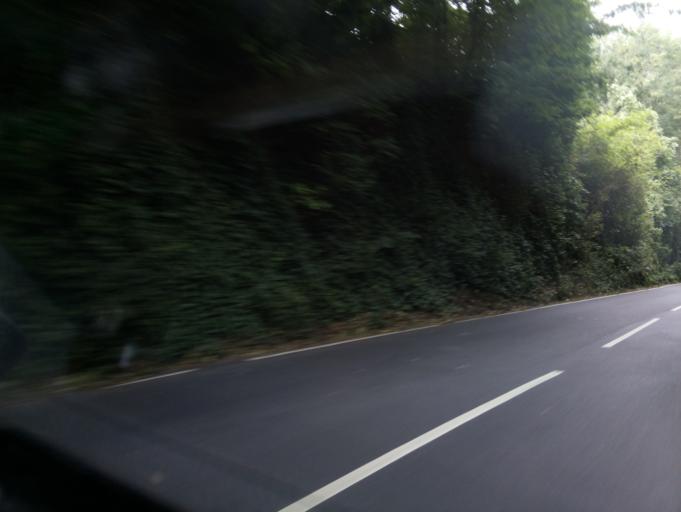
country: GB
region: England
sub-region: Devon
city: Starcross
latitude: 50.6415
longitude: -3.4748
